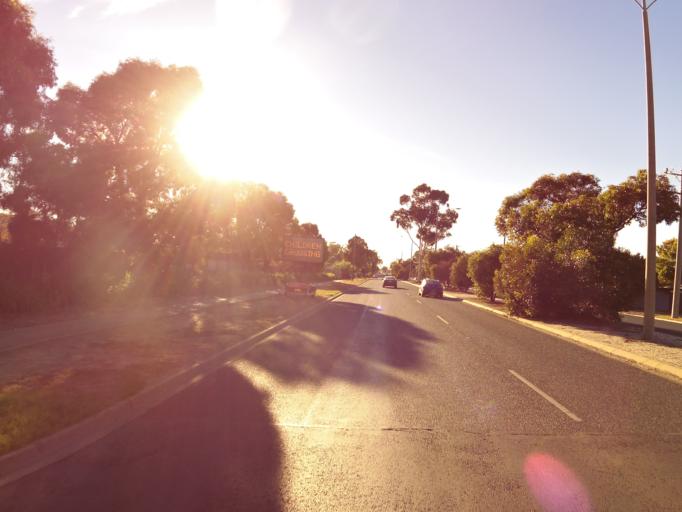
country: AU
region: Victoria
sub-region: Campaspe
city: Echuca
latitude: -36.1404
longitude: 144.7363
